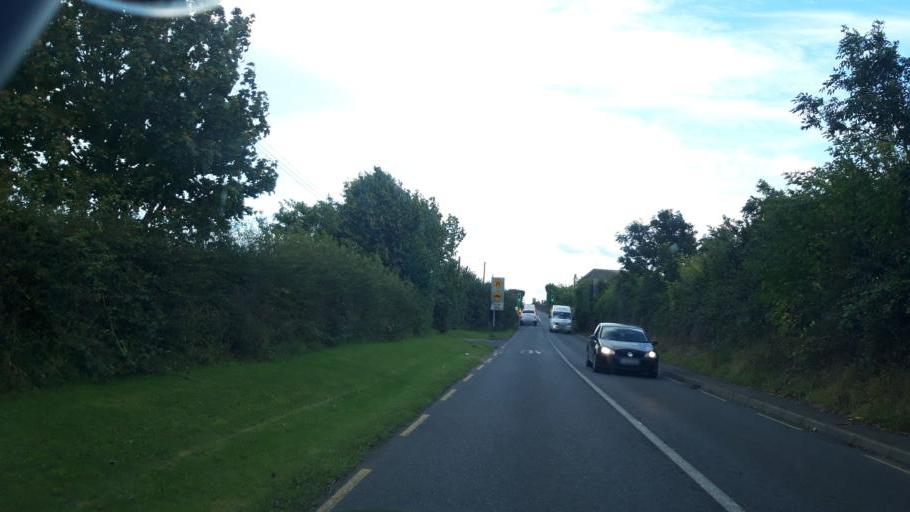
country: IE
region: Leinster
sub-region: South Dublin
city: Newcastle
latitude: 53.3190
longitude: -6.5199
